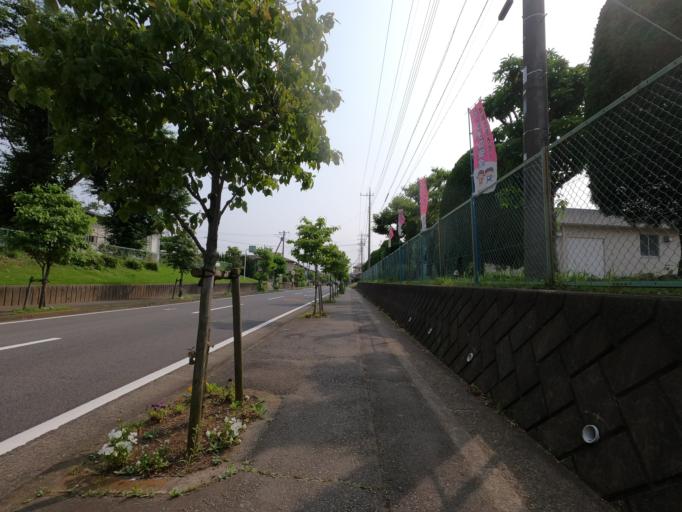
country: JP
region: Ibaraki
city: Moriya
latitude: 35.9639
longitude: 139.9743
